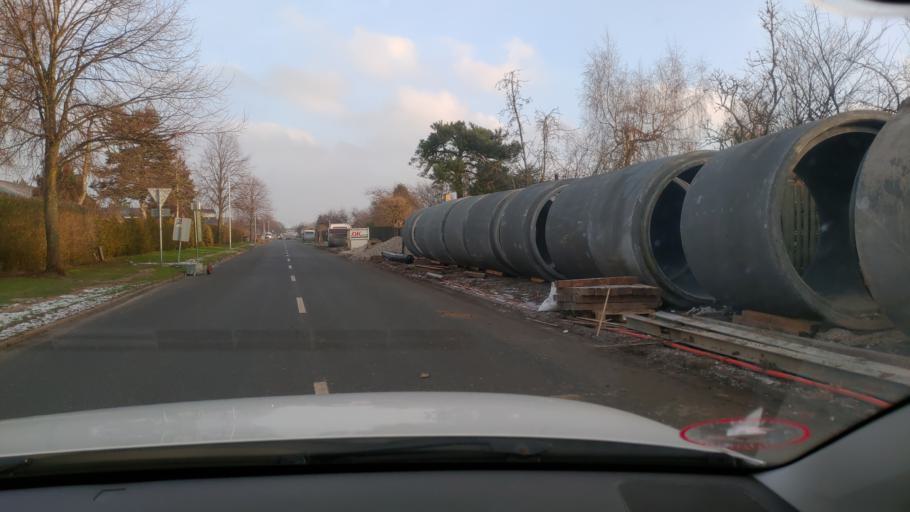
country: DK
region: Zealand
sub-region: Solrod Kommune
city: Solrod Strand
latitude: 55.5385
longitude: 12.2191
